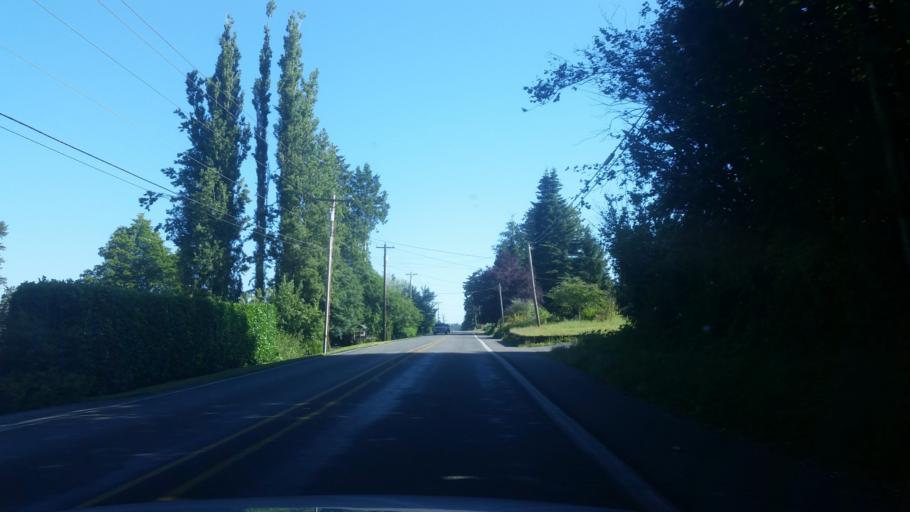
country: US
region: Washington
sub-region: Snohomish County
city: Cathcart
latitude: 47.8639
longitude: -122.0991
